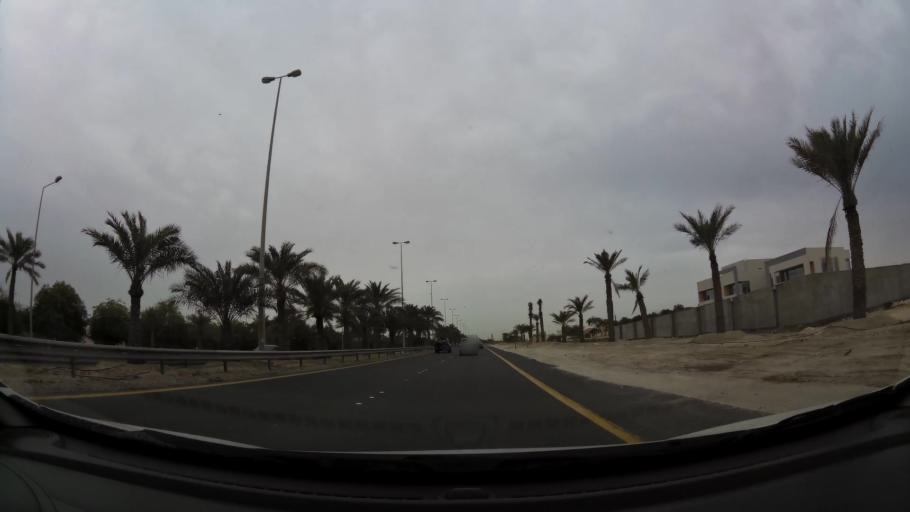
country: BH
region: Northern
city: Ar Rifa'
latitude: 26.1435
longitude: 50.5398
